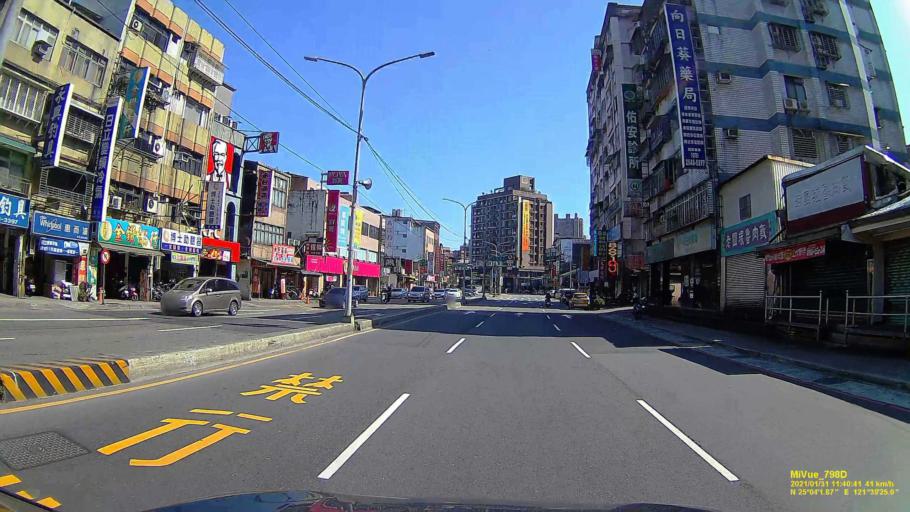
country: TW
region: Taiwan
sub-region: Keelung
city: Keelung
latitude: 25.0672
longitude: 121.6574
